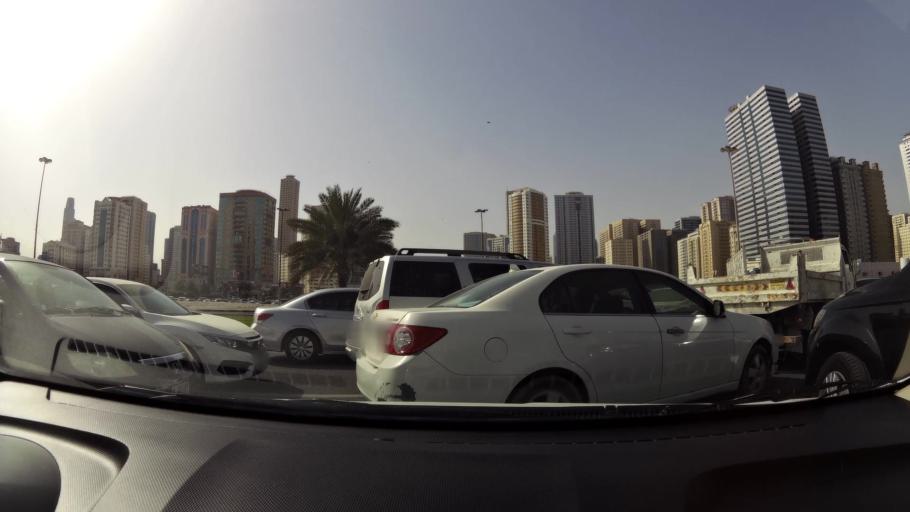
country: AE
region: Ash Shariqah
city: Sharjah
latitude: 25.3067
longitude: 55.3723
